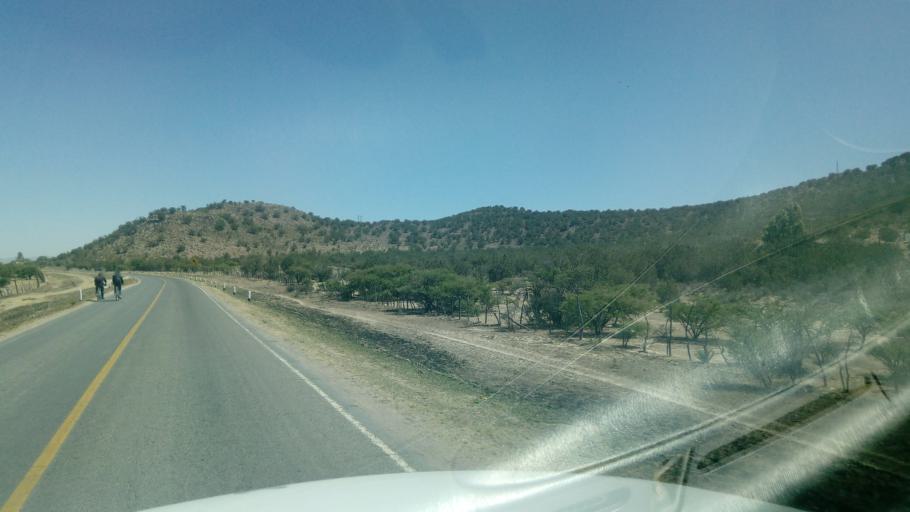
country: MX
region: Durango
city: Victoria de Durango
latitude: 24.1595
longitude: -104.7043
